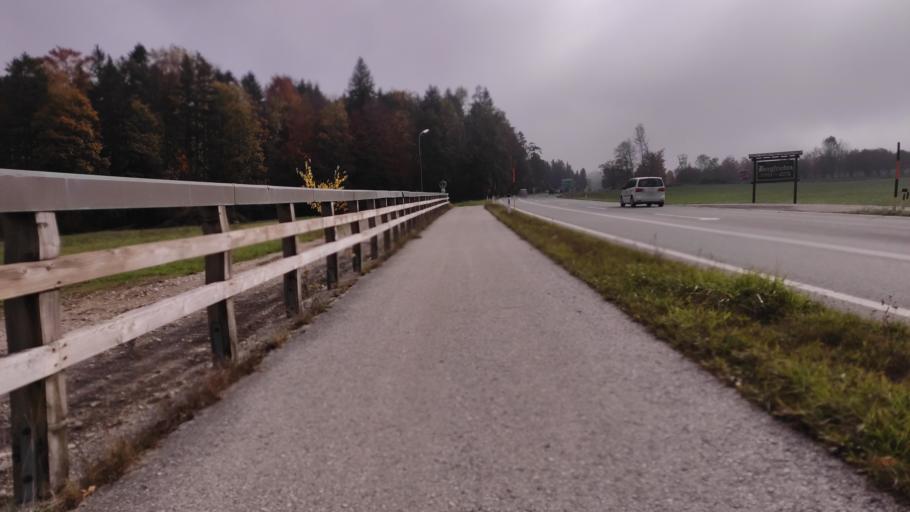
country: AT
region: Upper Austria
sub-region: Politischer Bezirk Gmunden
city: Sankt Wolfgang im Salzkammergut
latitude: 47.7333
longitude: 13.4138
